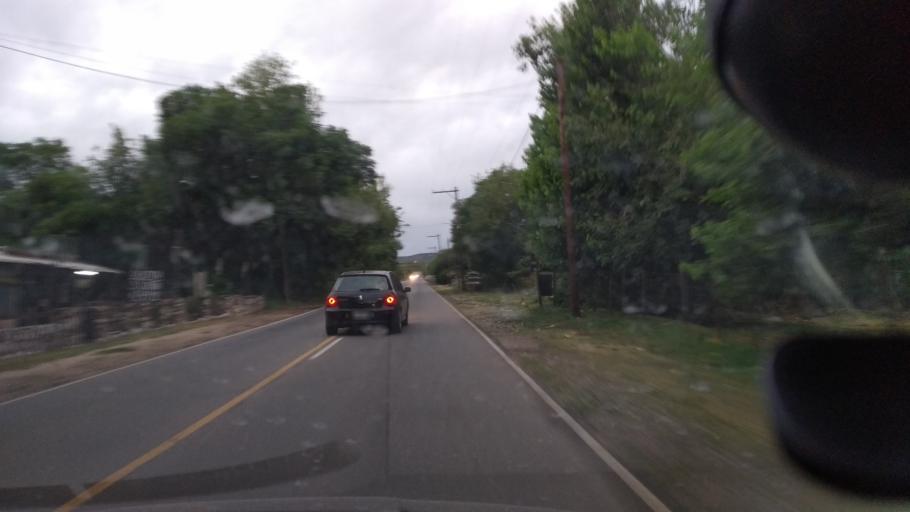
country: AR
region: Cordoba
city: Villa Las Rosas
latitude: -31.9350
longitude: -65.0405
